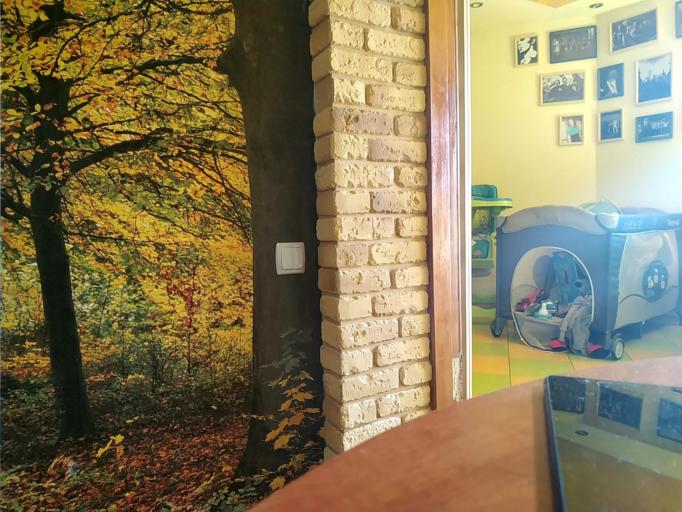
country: RU
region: Tverskaya
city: Torzhok
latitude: 57.0260
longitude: 35.0330
